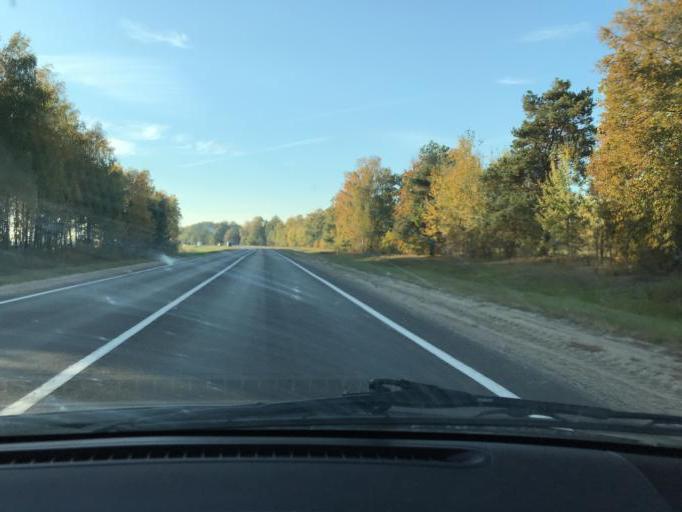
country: BY
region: Brest
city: Horad Kobryn
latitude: 52.2172
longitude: 24.5477
